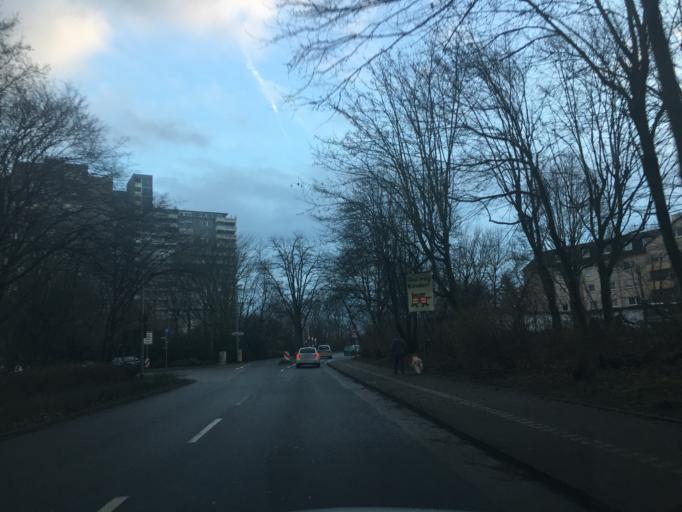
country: DE
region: Hesse
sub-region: Regierungsbezirk Darmstadt
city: Hattersheim
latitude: 50.0737
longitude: 8.5010
